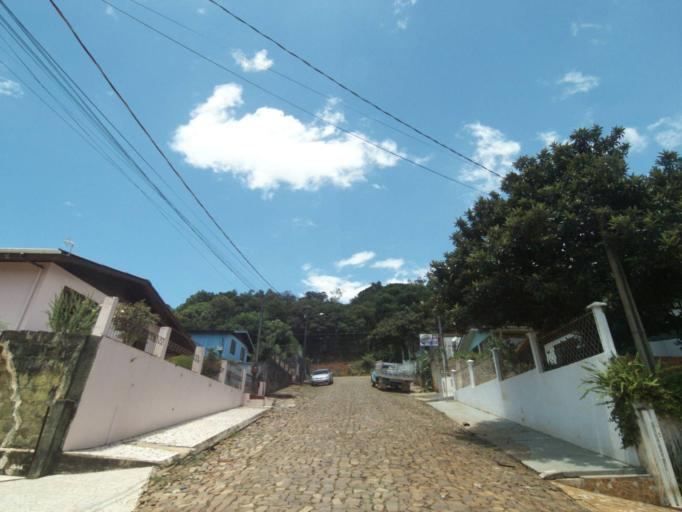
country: BR
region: Parana
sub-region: Uniao Da Vitoria
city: Uniao da Vitoria
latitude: -26.1579
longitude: -51.5525
